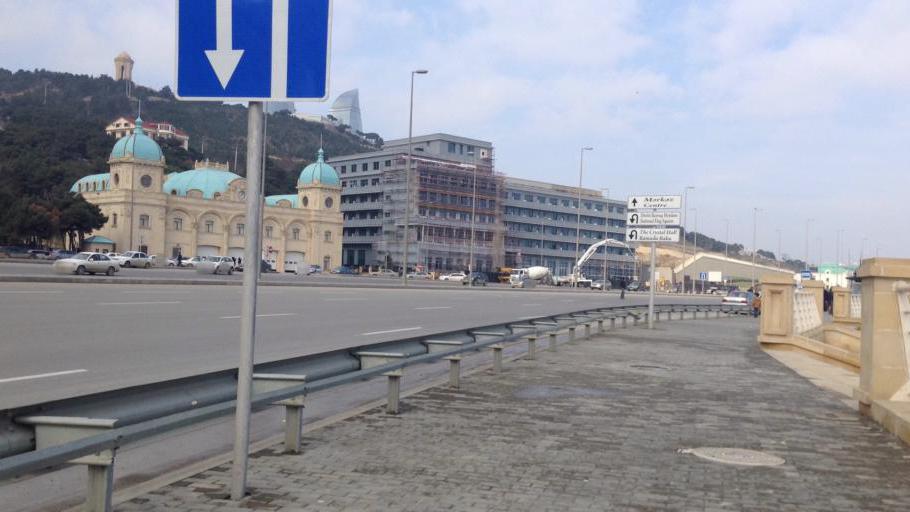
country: AZ
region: Baki
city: Badamdar
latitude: 40.3524
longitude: 49.8346
